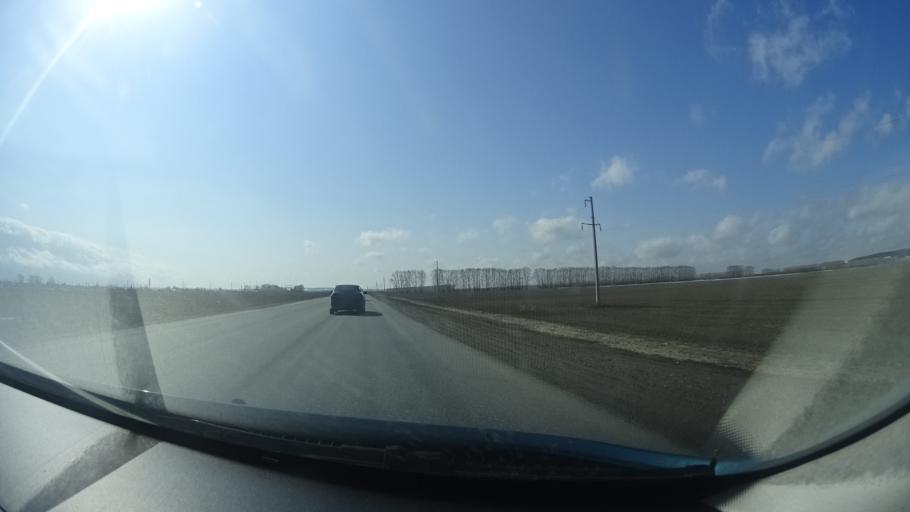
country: RU
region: Bashkortostan
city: Mikhaylovka
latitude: 54.9635
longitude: 55.7611
